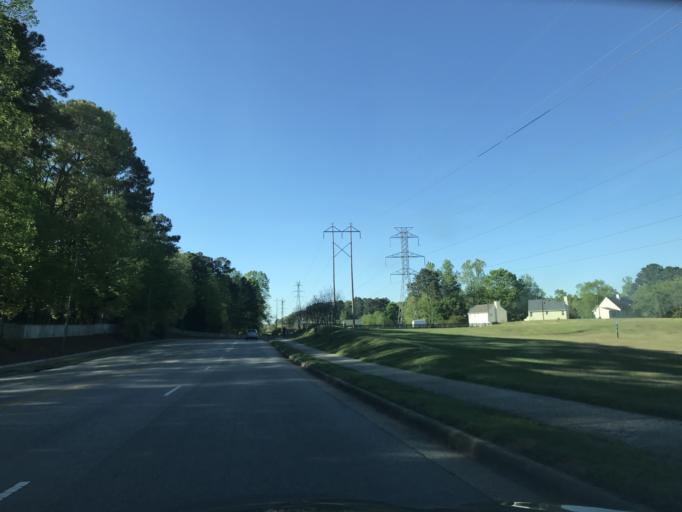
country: US
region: North Carolina
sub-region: Wake County
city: Knightdale
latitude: 35.8066
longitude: -78.5558
